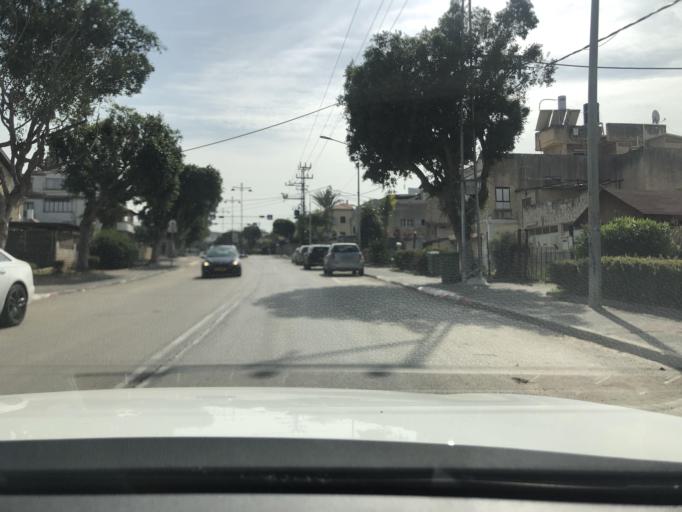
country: IL
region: Central District
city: Rosh Ha'Ayin
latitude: 32.0909
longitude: 34.9481
